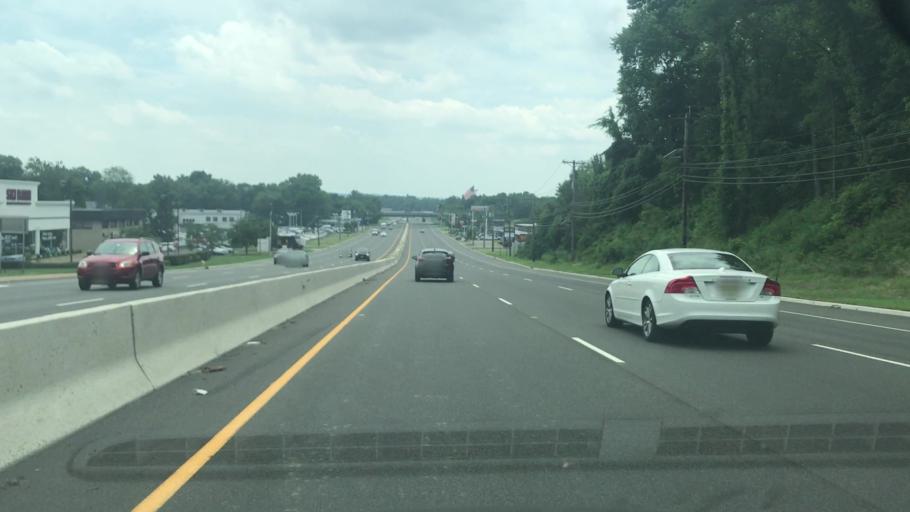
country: US
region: New Jersey
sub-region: Passaic County
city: Wayne
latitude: 40.9297
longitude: -74.2688
